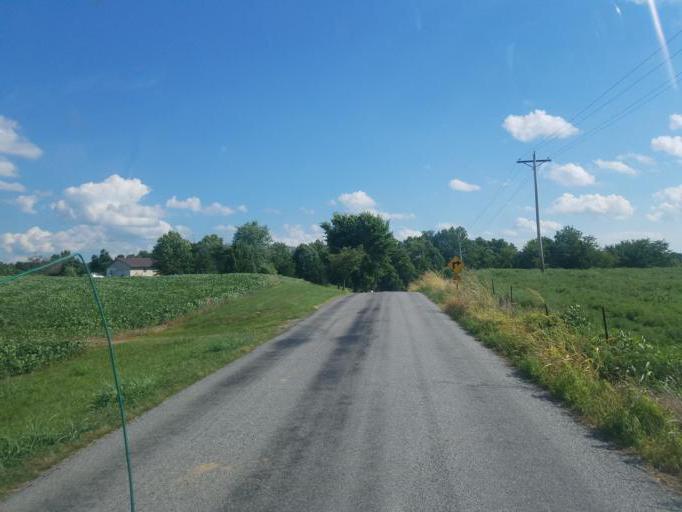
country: US
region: Illinois
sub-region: Jackson County
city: Murphysboro
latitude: 37.7111
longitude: -89.3005
